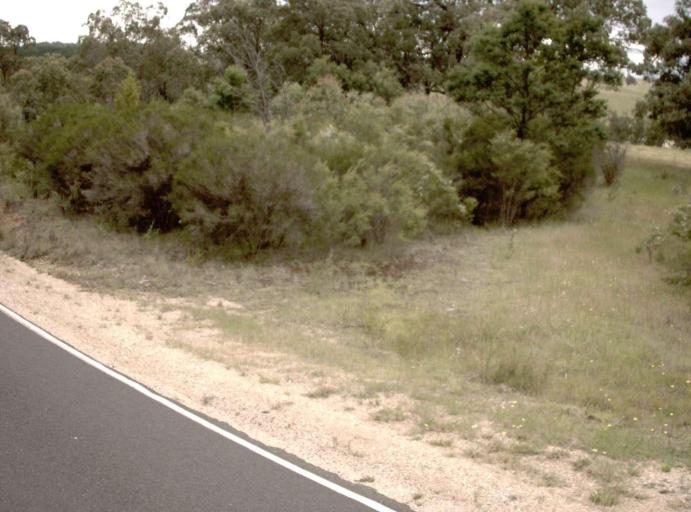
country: AU
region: Victoria
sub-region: East Gippsland
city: Bairnsdale
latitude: -37.7370
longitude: 147.3120
